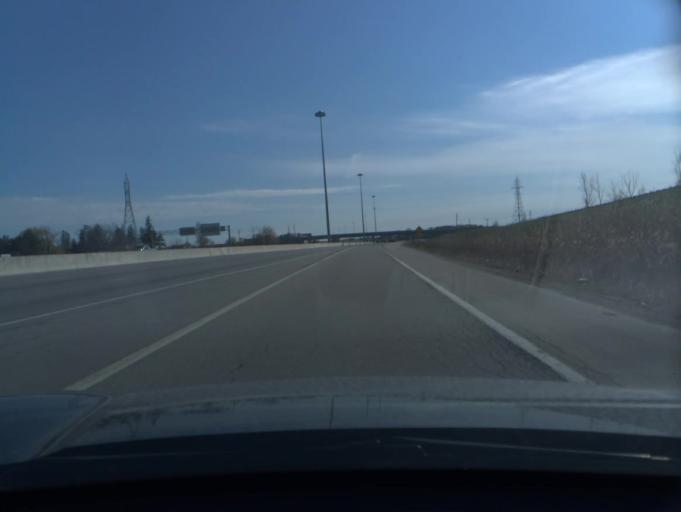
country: CA
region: Ontario
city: North Perth
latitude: 43.8068
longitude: -80.9999
